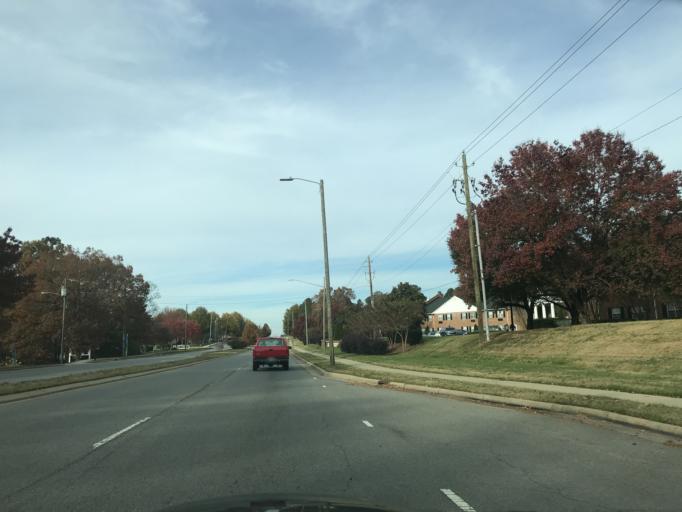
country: US
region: North Carolina
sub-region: Wake County
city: West Raleigh
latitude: 35.8942
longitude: -78.6802
